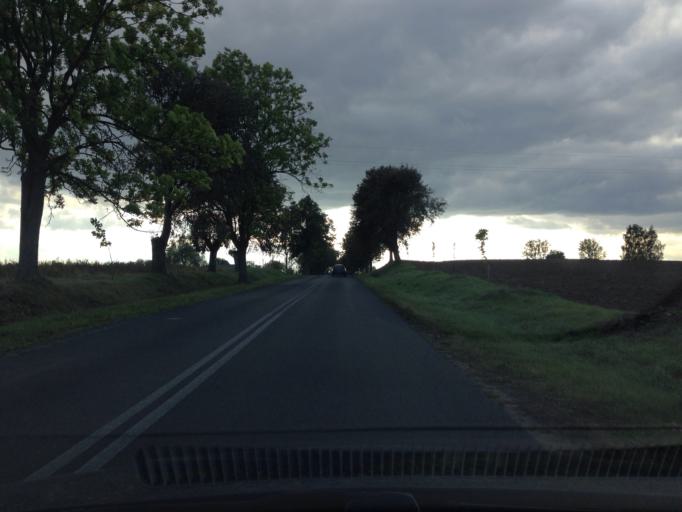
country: PL
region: Kujawsko-Pomorskie
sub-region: Powiat rypinski
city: Rogowo
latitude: 52.9850
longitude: 19.3374
